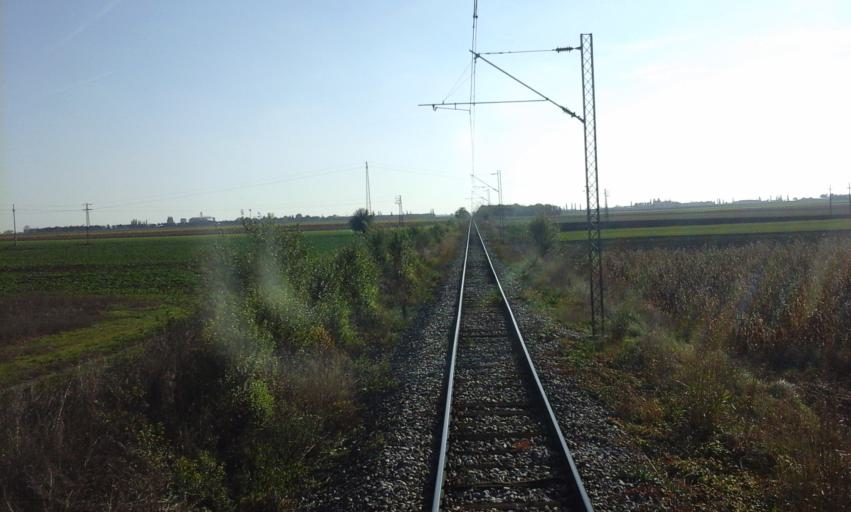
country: RS
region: Autonomna Pokrajina Vojvodina
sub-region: Severnobacki Okrug
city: Backa Topola
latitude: 45.7932
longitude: 19.6474
